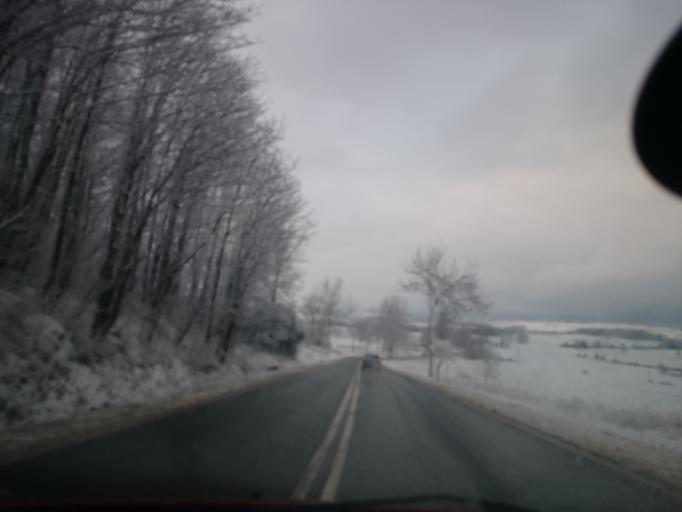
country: PL
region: Lower Silesian Voivodeship
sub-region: Powiat klodzki
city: Bystrzyca Klodzka
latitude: 50.3505
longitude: 16.6644
